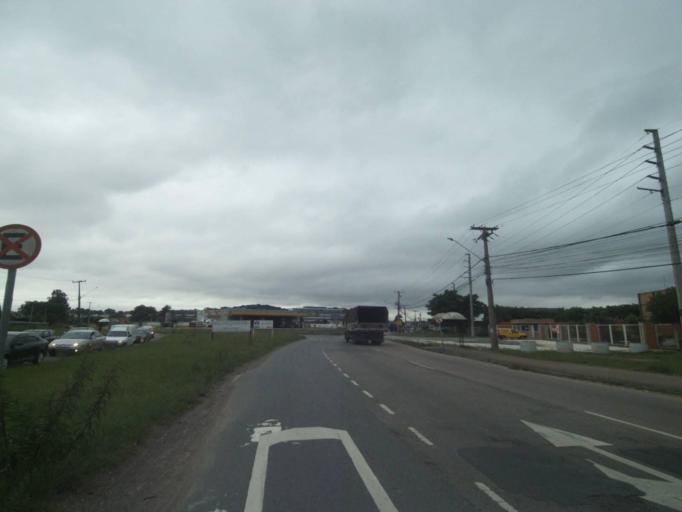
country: BR
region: Parana
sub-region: Curitiba
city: Curitiba
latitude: -25.5204
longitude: -49.3290
